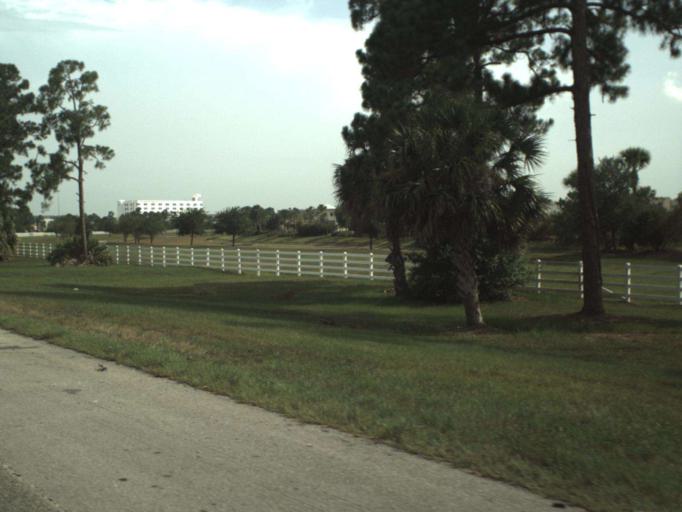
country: US
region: Florida
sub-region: Saint Lucie County
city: Port Saint Lucie
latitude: 27.2705
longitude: -80.4247
